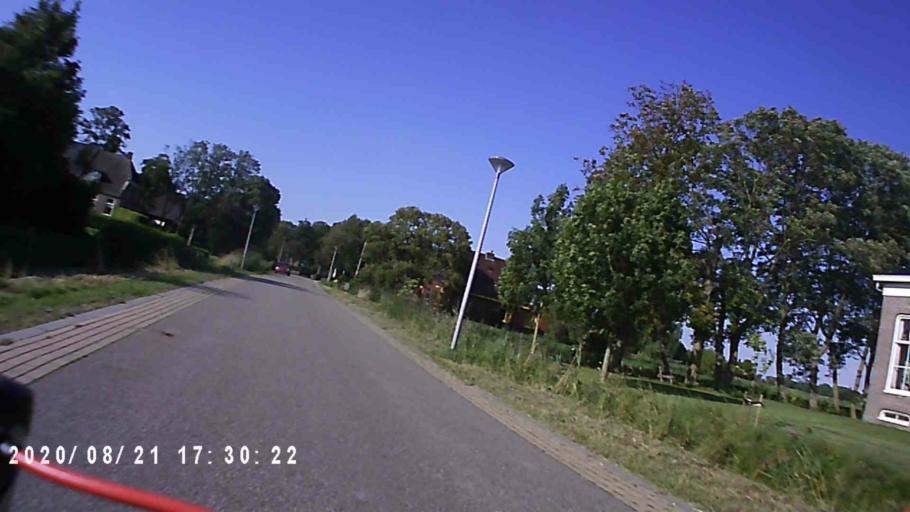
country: NL
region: Groningen
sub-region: Gemeente Bedum
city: Bedum
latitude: 53.2699
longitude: 6.5890
